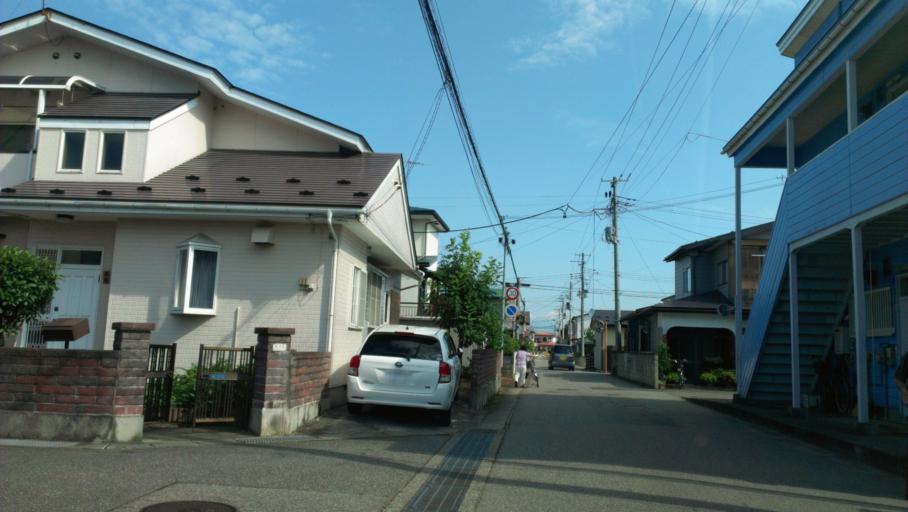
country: JP
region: Fukushima
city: Kitakata
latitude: 37.4985
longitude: 139.9168
